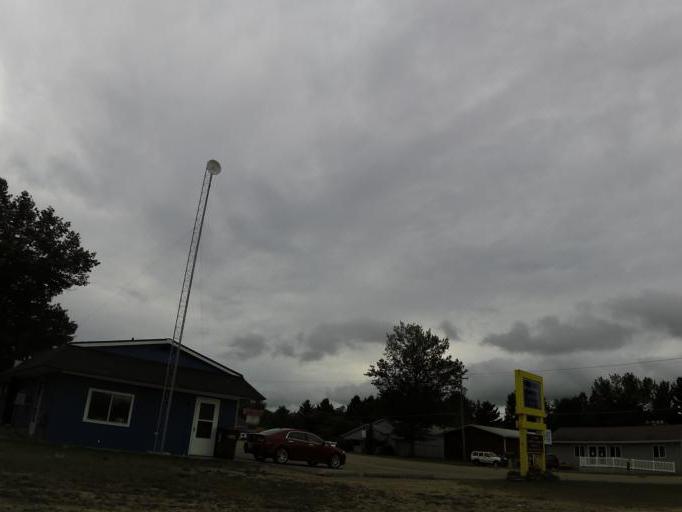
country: US
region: Michigan
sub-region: Roscommon County
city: Saint Helen
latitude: 44.3576
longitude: -84.4098
